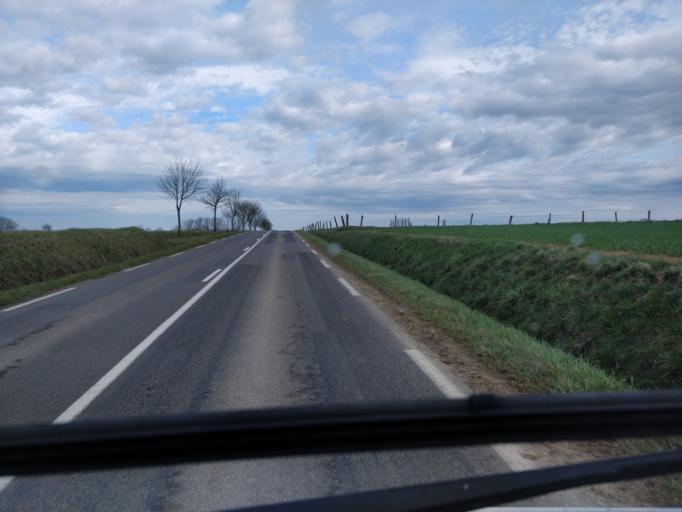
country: FR
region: Lorraine
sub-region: Departement de Meurthe-et-Moselle
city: Doncourt-les-Conflans
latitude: 49.0705
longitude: 5.8868
